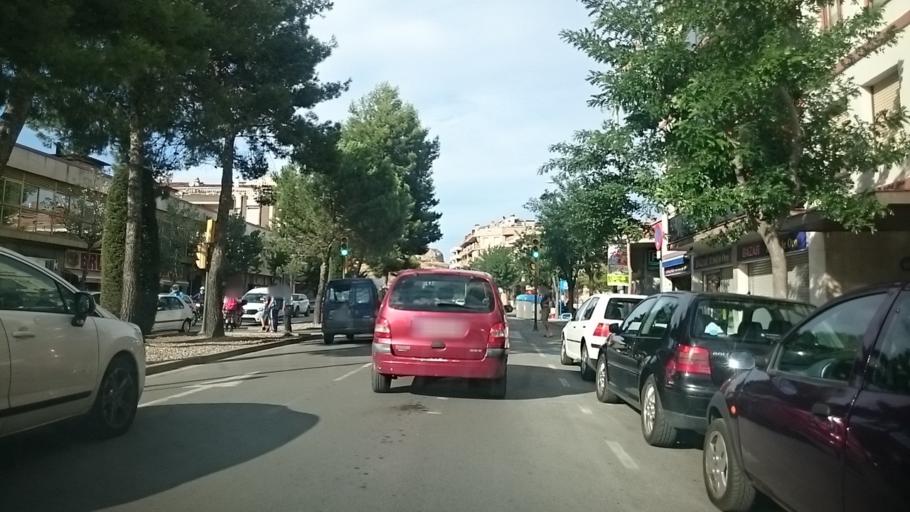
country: ES
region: Catalonia
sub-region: Provincia de Barcelona
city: Igualada
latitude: 41.5865
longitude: 1.6142
